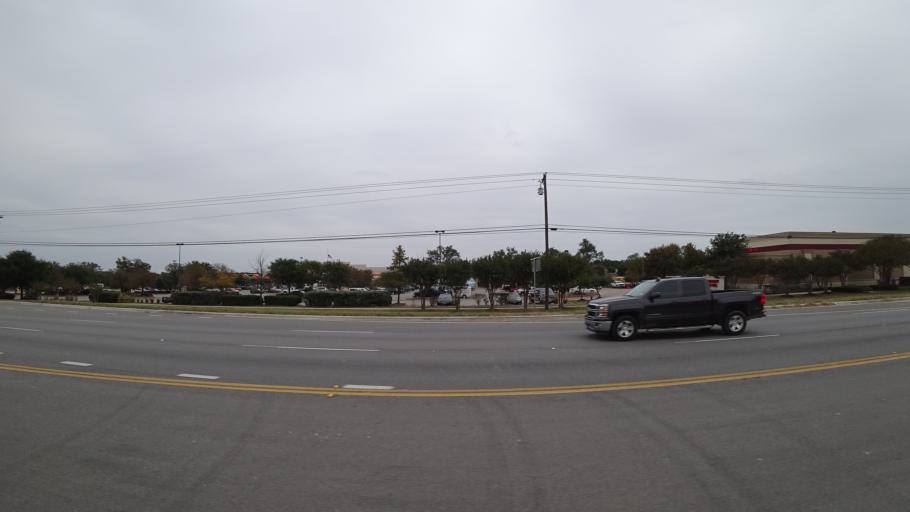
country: US
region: Texas
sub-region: Williamson County
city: Cedar Park
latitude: 30.5327
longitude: -97.7892
